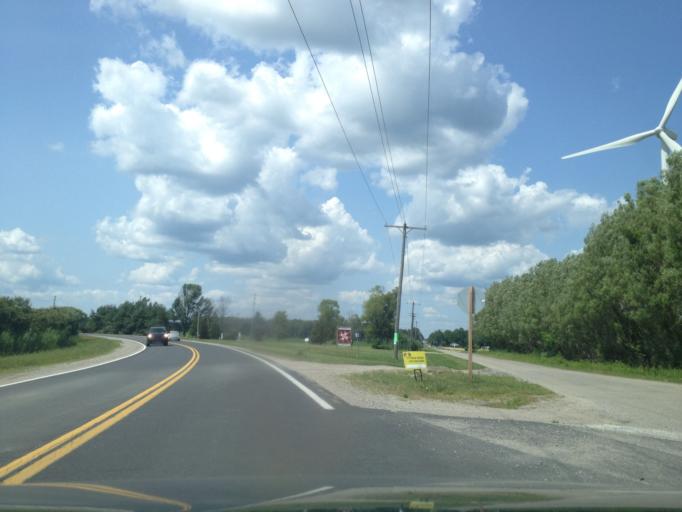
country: CA
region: Ontario
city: Aylmer
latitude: 42.6594
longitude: -80.8101
